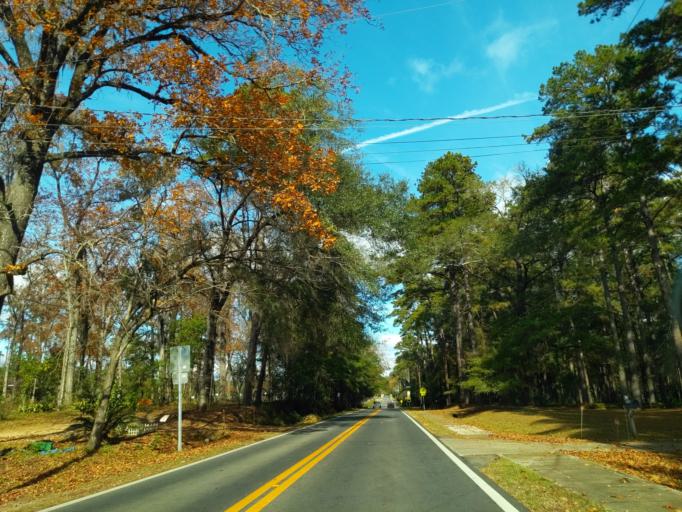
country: US
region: Florida
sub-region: Leon County
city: Tallahassee
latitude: 30.4713
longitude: -84.2102
